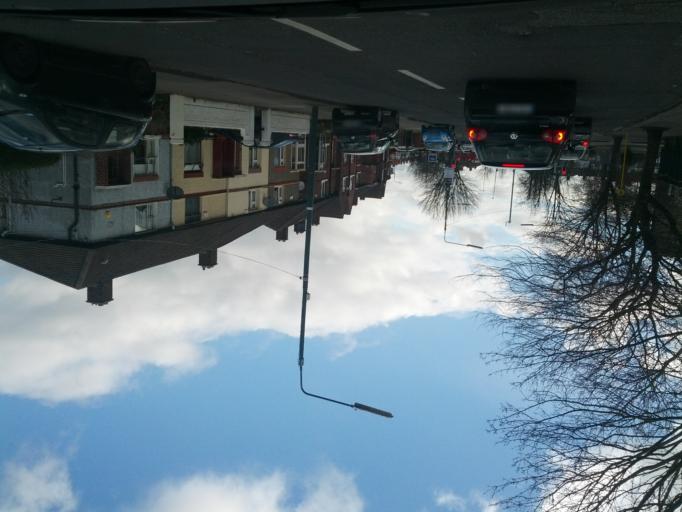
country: IE
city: Donnycarney
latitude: 53.3747
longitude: -6.2165
